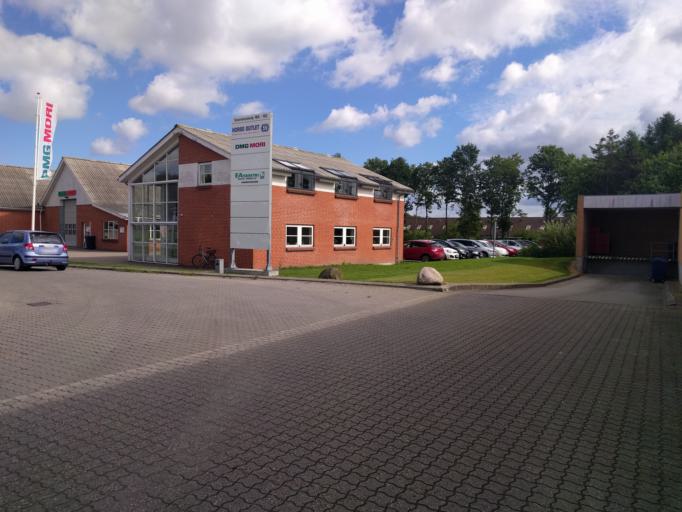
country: DK
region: South Denmark
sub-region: Fredericia Kommune
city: Snoghoj
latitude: 55.5363
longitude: 9.7181
